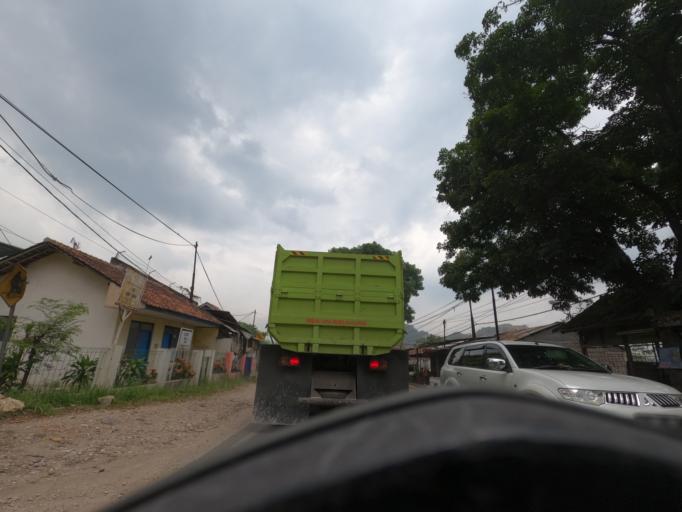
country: ID
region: West Java
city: Padalarang
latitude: -6.8309
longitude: 107.4329
